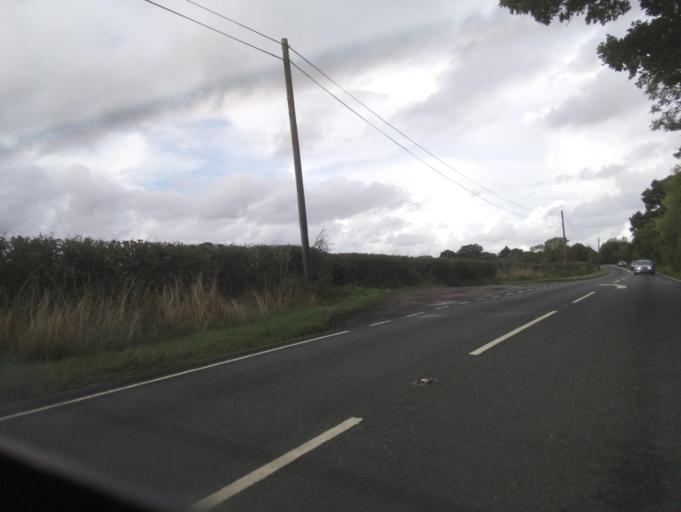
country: GB
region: England
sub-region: Worcestershire
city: Droitwich
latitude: 52.3007
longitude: -2.1750
